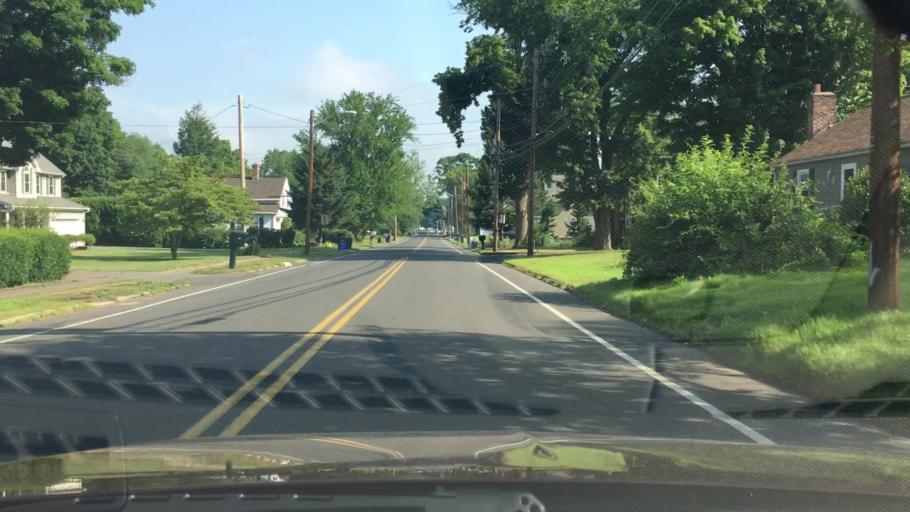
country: US
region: Massachusetts
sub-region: Hampden County
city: East Longmeadow
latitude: 42.0609
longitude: -72.5122
